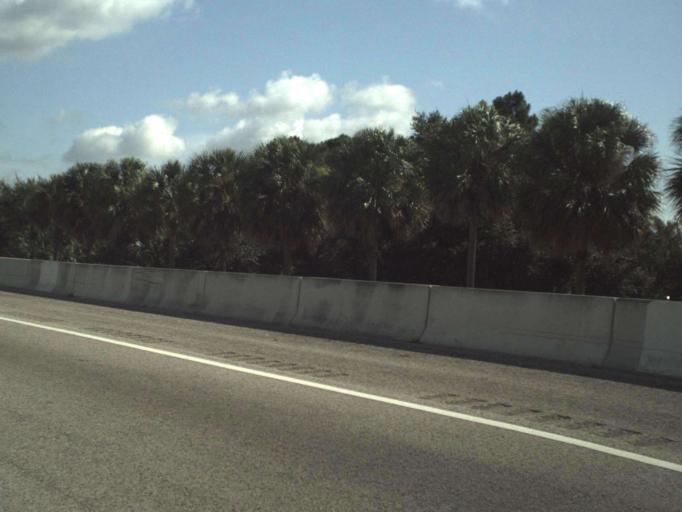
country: US
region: Florida
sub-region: Palm Beach County
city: North Palm Beach
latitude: 26.8341
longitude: -80.0982
